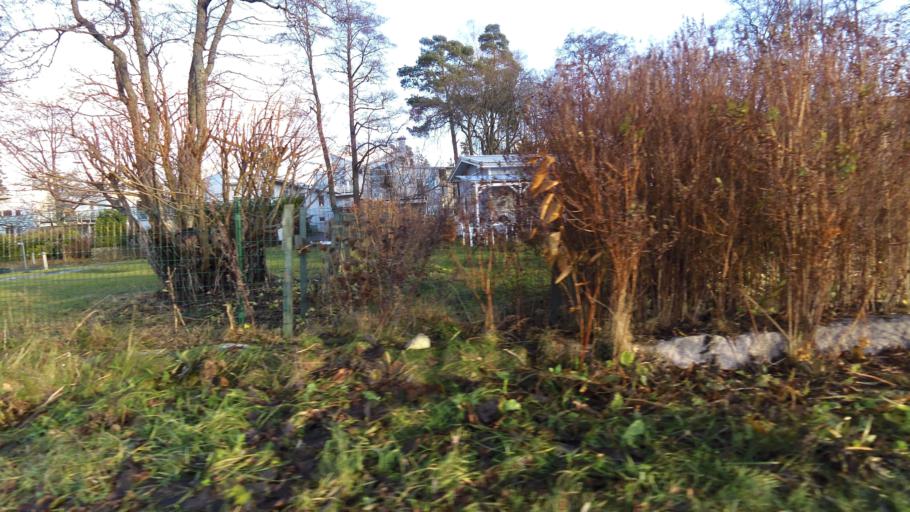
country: FI
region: Uusimaa
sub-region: Helsinki
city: Koukkuniemi
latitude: 60.1497
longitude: 24.7344
